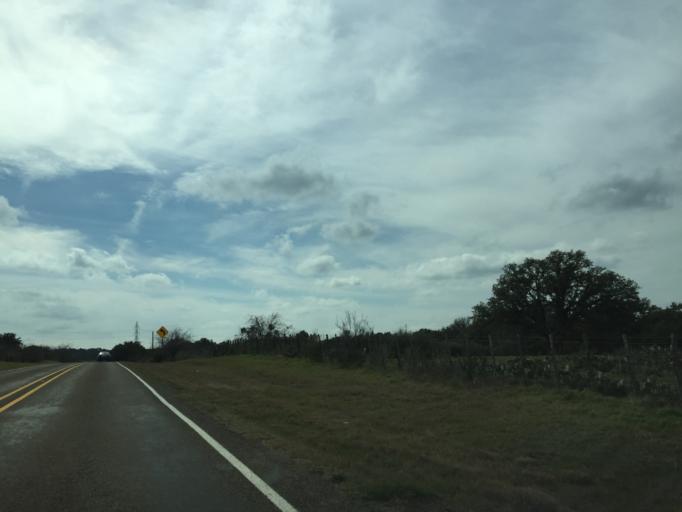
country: US
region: Texas
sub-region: Burnet County
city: Granite Shoals
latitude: 30.5282
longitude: -98.4464
